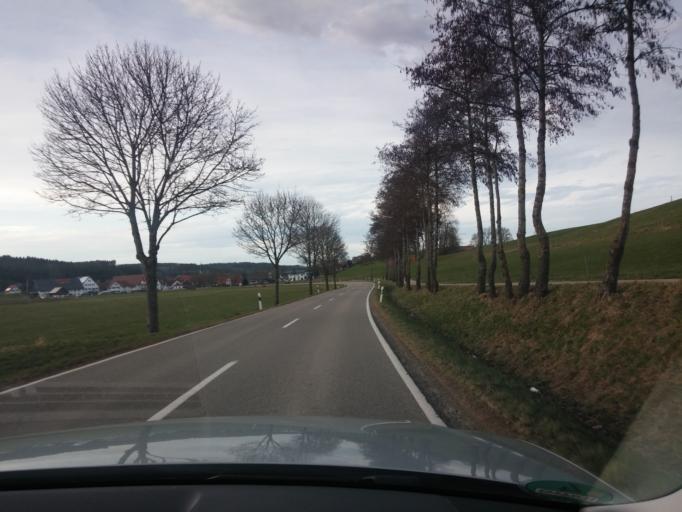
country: DE
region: Bavaria
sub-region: Swabia
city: Woringen
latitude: 47.8928
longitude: 10.2105
